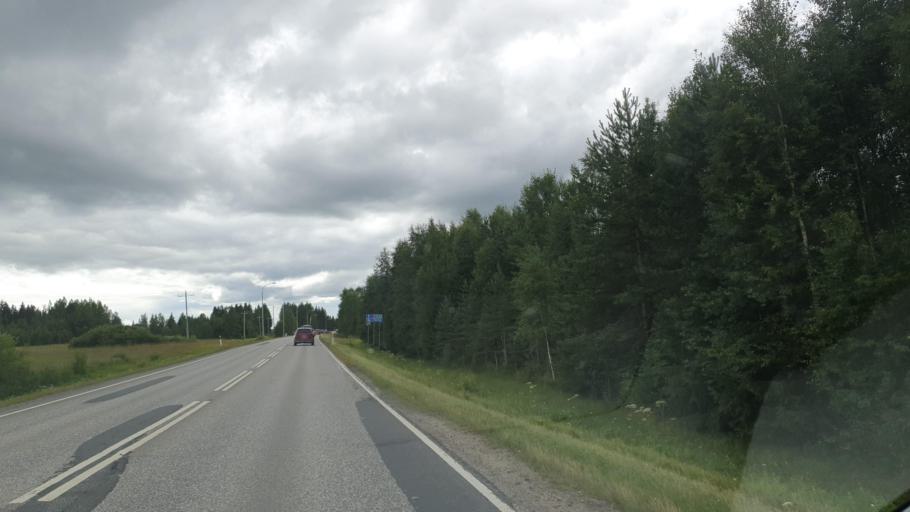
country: FI
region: Northern Savo
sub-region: Ylae-Savo
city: Sonkajaervi
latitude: 63.7287
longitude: 27.3745
